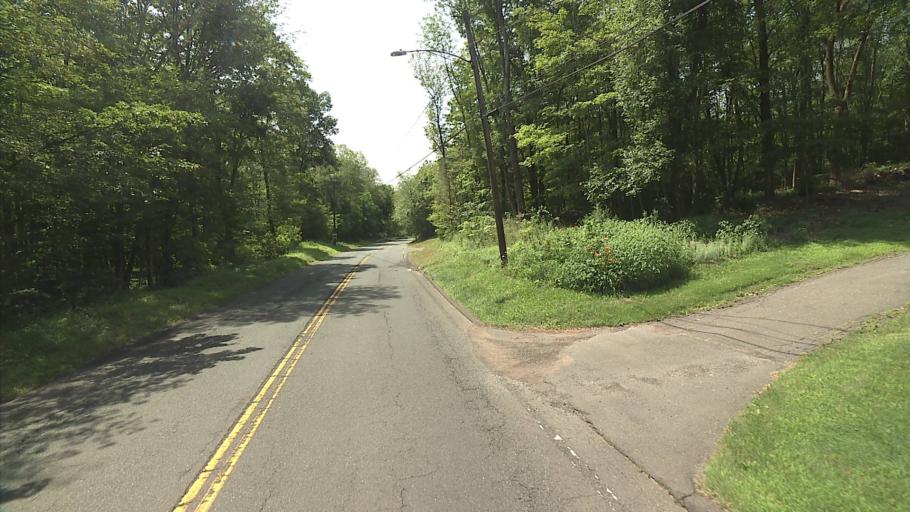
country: US
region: Connecticut
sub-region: New Haven County
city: Meriden
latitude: 41.5672
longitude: -72.8080
